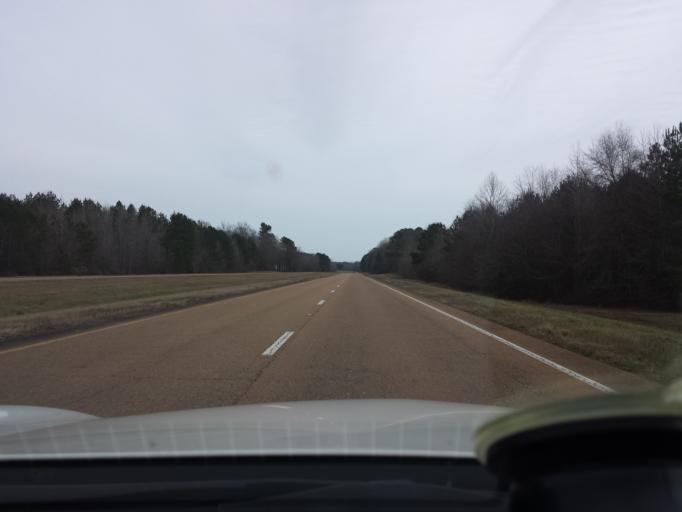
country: US
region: Mississippi
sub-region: Winston County
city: Louisville
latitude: 33.0696
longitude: -89.1268
